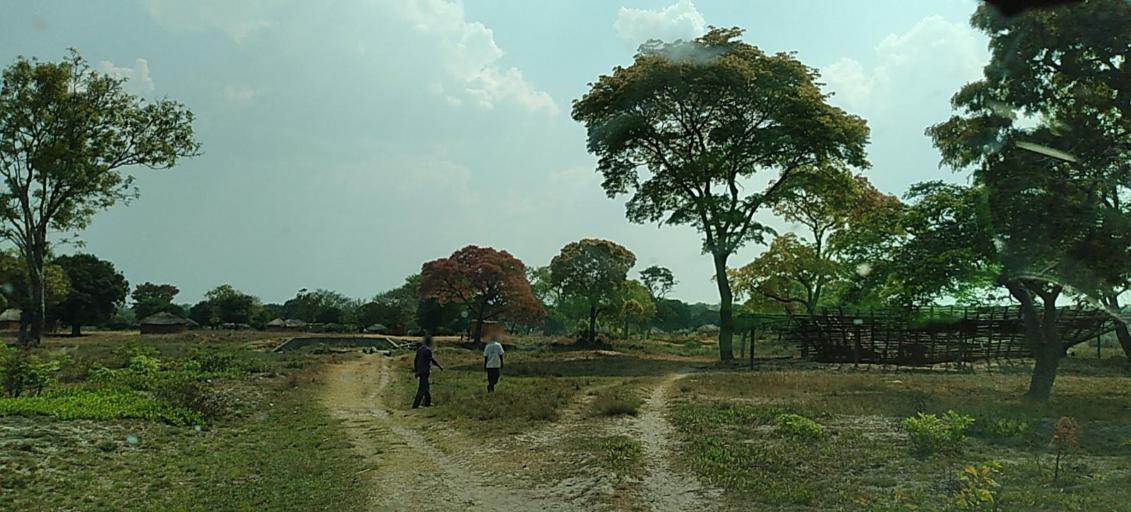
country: ZM
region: North-Western
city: Kabompo
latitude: -13.4477
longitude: 23.6637
